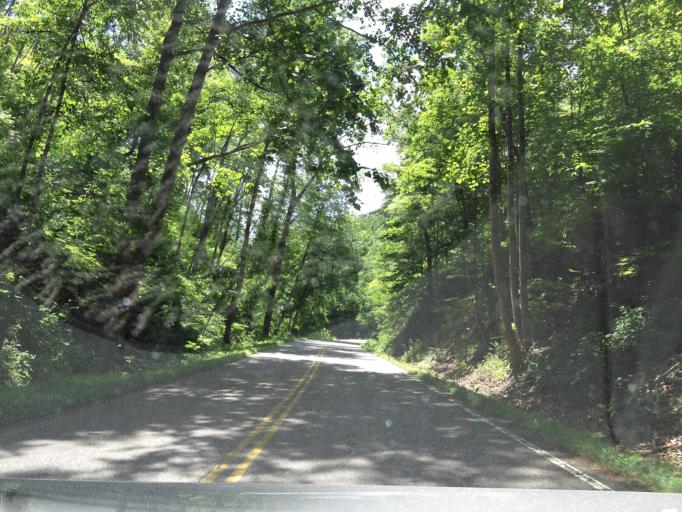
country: US
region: Tennessee
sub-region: Loudon County
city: Greenback
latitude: 35.5179
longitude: -83.9888
